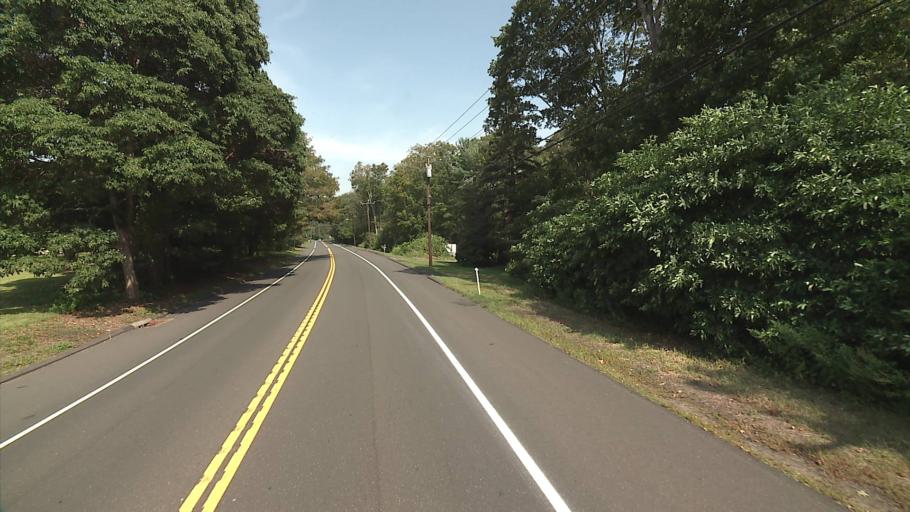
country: US
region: Connecticut
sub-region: New Haven County
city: Guilford
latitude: 41.3677
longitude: -72.6379
